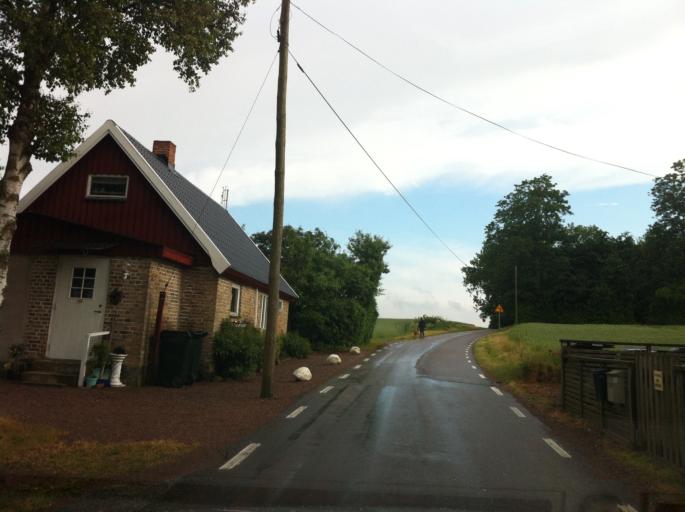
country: SE
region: Skane
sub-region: Helsingborg
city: Glumslov
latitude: 55.9430
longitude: 12.8407
